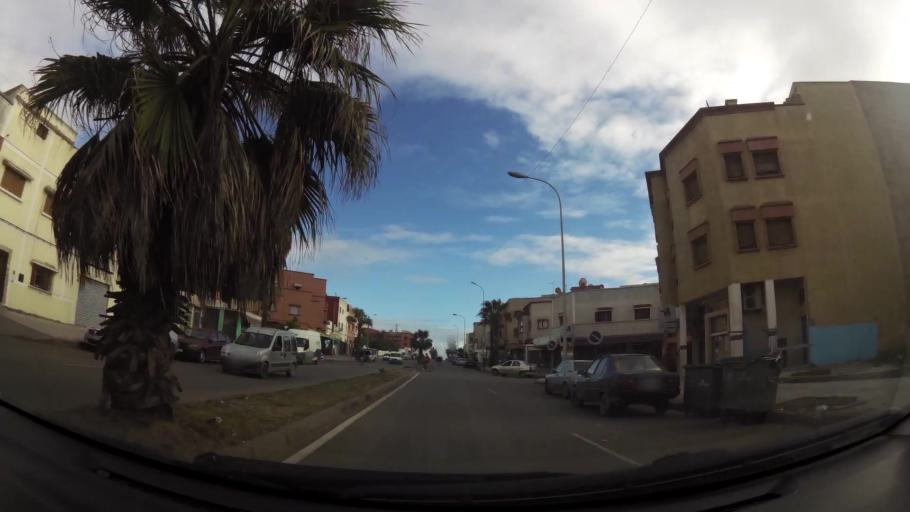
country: MA
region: Doukkala-Abda
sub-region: El-Jadida
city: El Jadida
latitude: 33.2539
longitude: -8.5183
